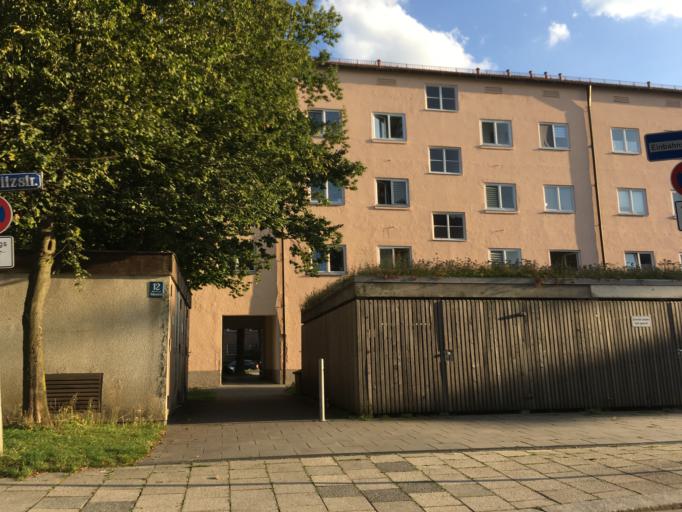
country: DE
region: Bavaria
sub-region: Upper Bavaria
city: Bogenhausen
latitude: 48.1213
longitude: 11.6145
